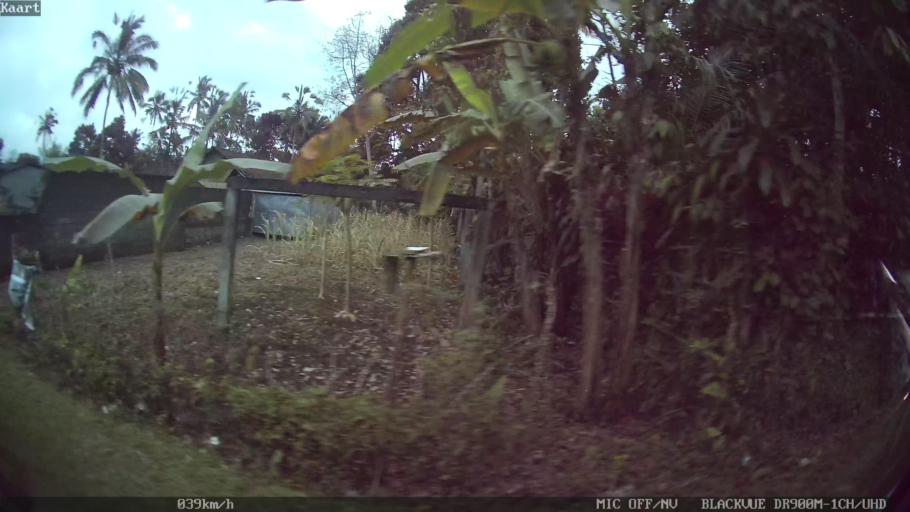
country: ID
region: Bali
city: Banjar Geriana Kangin
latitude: -8.3932
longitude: 115.4424
